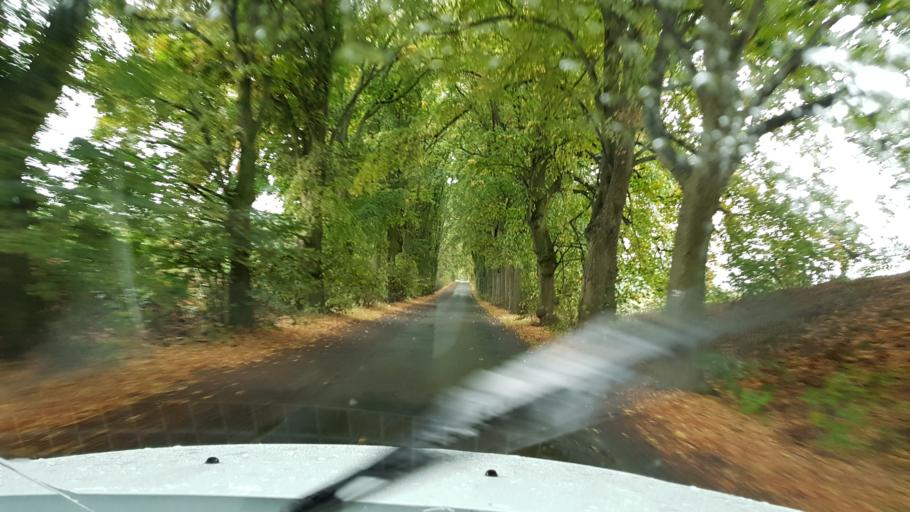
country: DE
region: Brandenburg
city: Schwedt (Oder)
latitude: 53.0076
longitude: 14.2960
